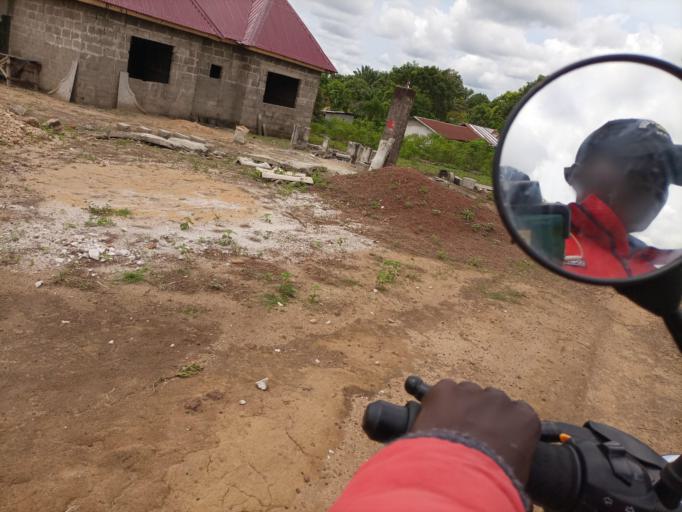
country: SL
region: Southern Province
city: Baoma
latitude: 7.9730
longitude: -11.7151
